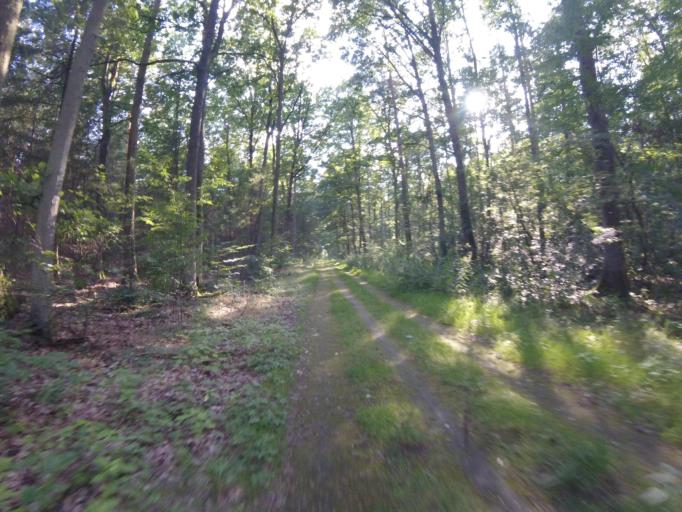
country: DE
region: Brandenburg
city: Schulzendorf
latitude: 52.3232
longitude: 13.5787
